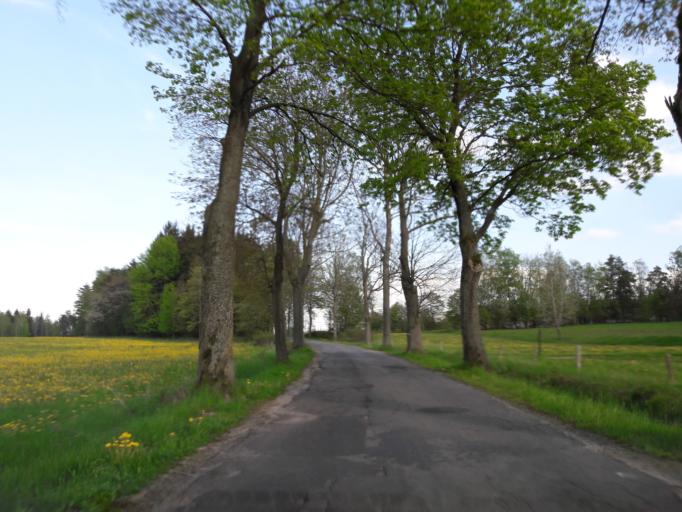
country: PL
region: Lower Silesian Voivodeship
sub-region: Powiat klodzki
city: Duszniki-Zdroj
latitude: 50.4224
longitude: 16.3795
